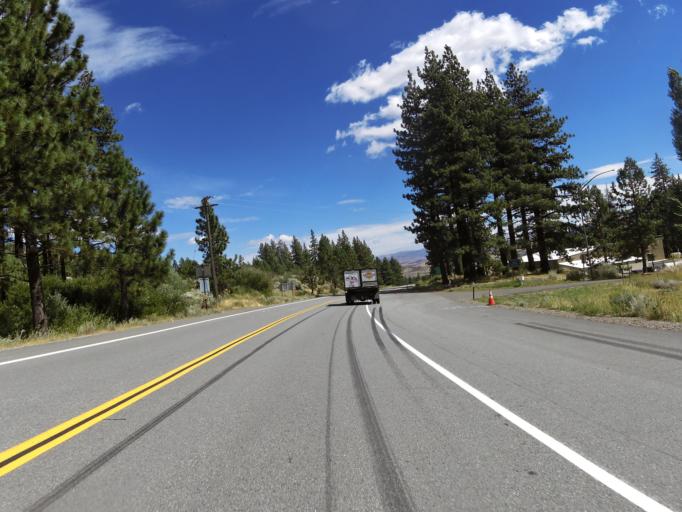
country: US
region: Nevada
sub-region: Douglas County
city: Gardnerville Ranchos
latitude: 38.7737
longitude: -119.8290
